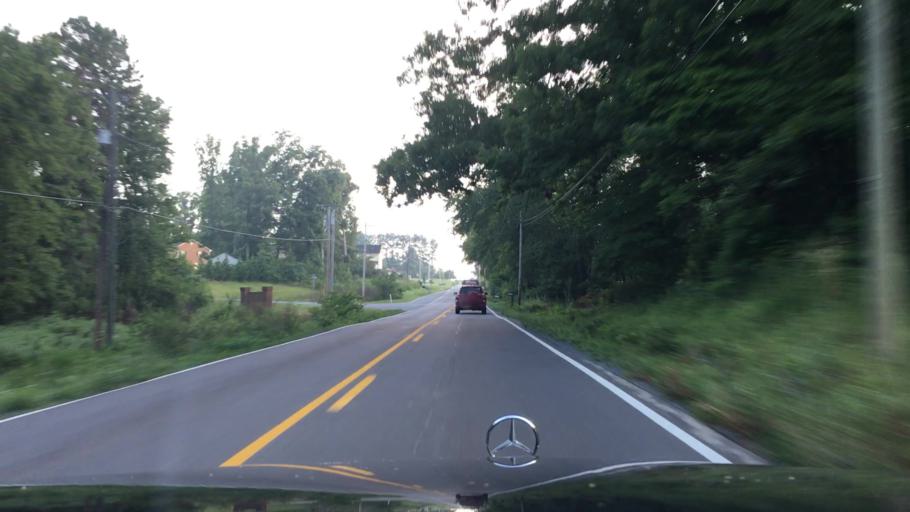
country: US
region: Virginia
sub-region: Campbell County
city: Timberlake
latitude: 37.3049
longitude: -79.2342
